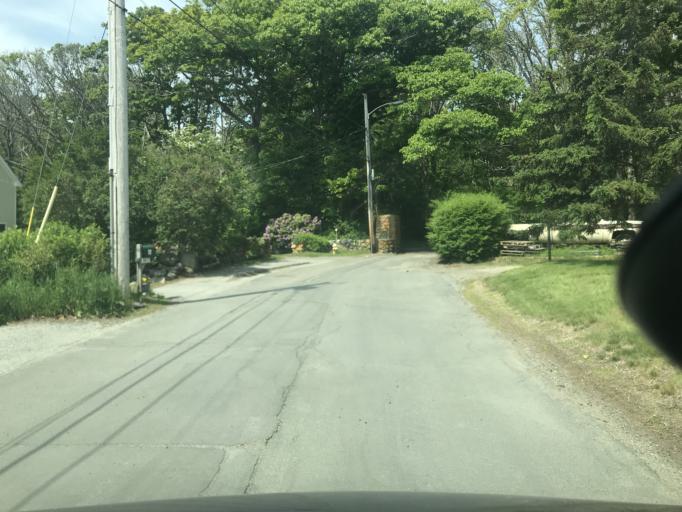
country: US
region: Massachusetts
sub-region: Essex County
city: Rockport
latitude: 42.6570
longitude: -70.6302
